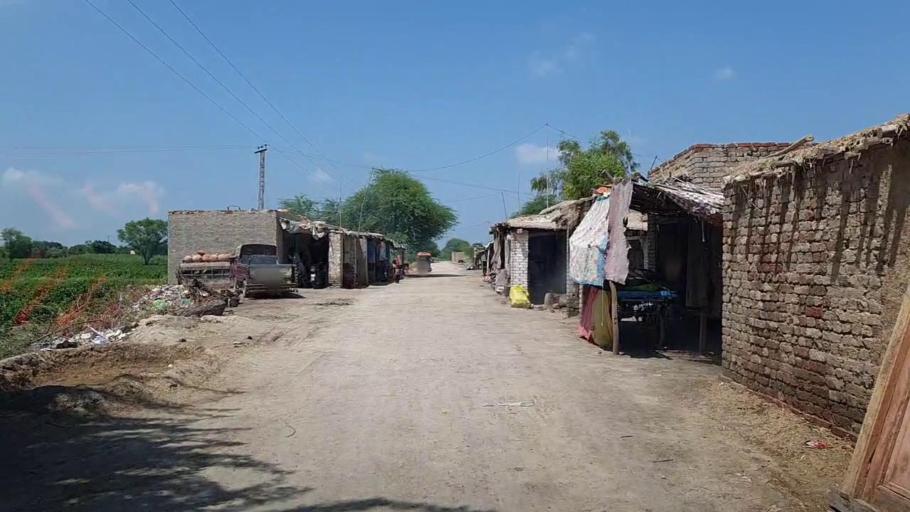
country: PK
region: Sindh
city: Kandiaro
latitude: 26.9858
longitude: 68.2456
